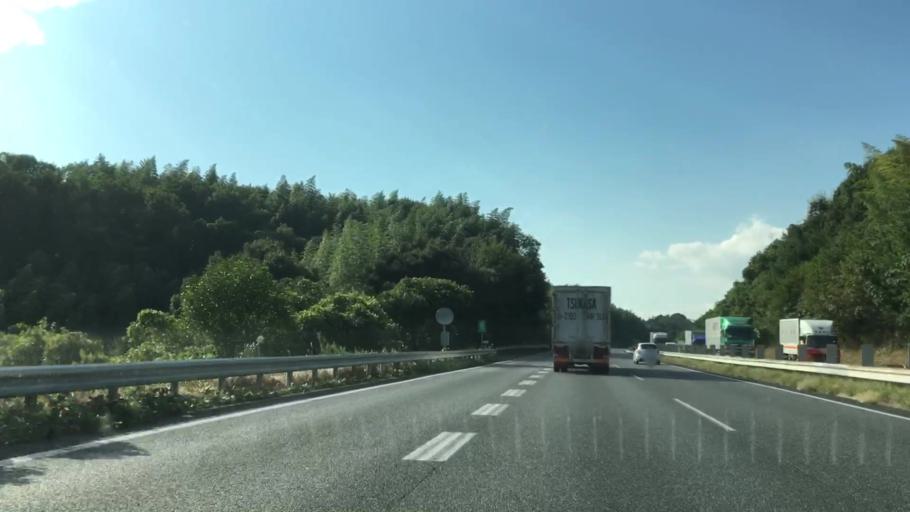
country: JP
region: Yamaguchi
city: Hikari
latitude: 34.0308
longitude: 131.9378
